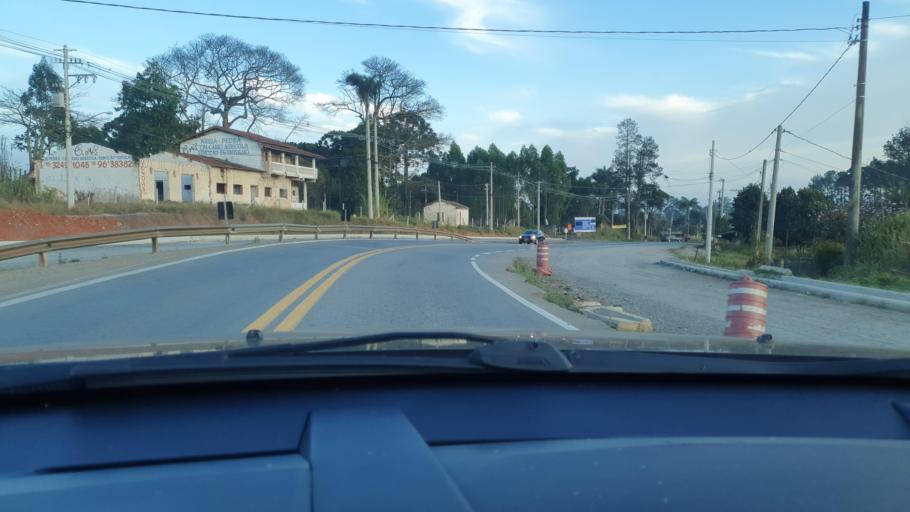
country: BR
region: Sao Paulo
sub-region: Ibiuna
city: Ibiuna
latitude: -23.6541
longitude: -47.1250
